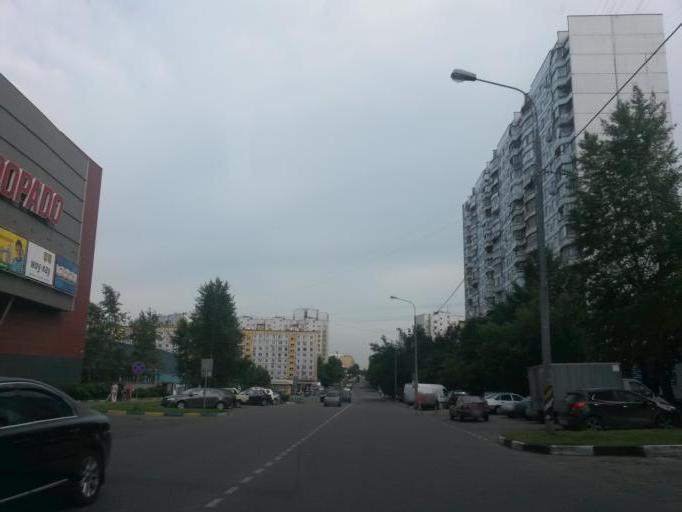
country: RU
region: Moscow
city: Orekhovo-Borisovo
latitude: 55.6119
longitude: 37.7309
